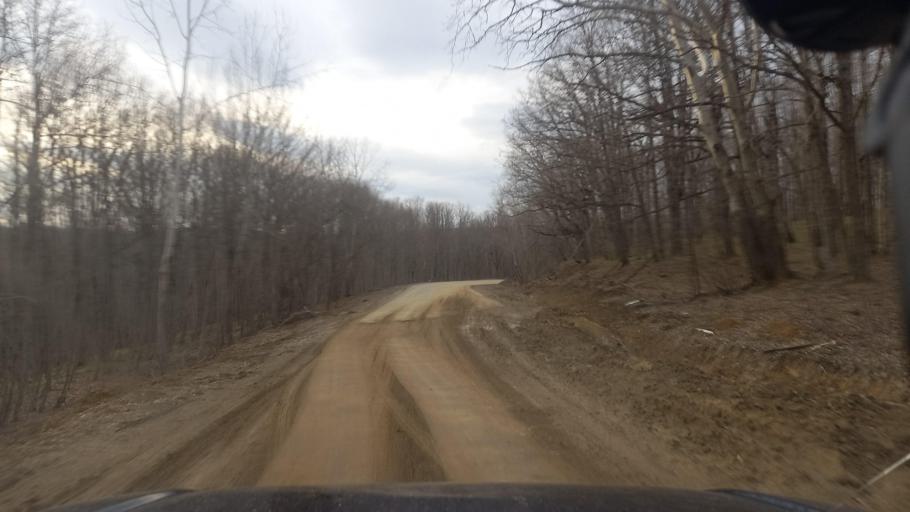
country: RU
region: Krasnodarskiy
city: Goryachiy Klyuch
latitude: 44.7003
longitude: 39.0191
